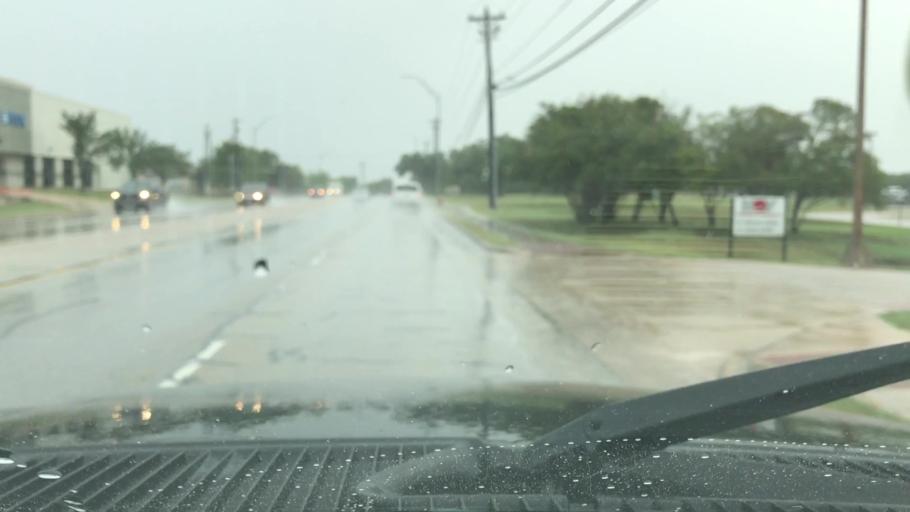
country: US
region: Texas
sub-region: Williamson County
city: Cedar Park
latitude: 30.4906
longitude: -97.8286
